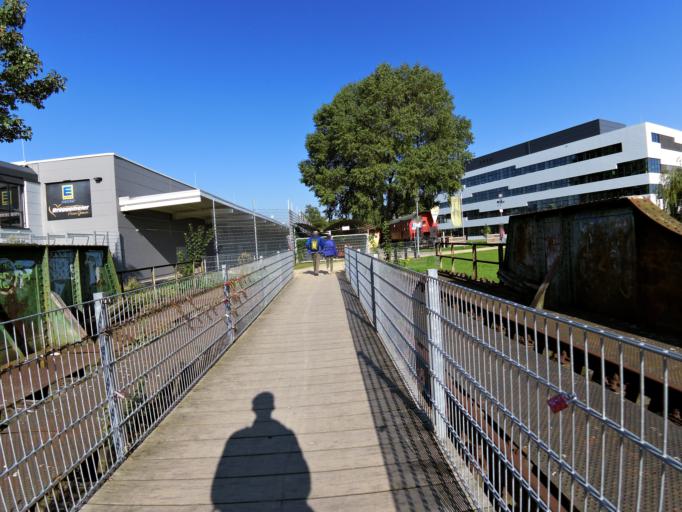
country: DE
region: North Rhine-Westphalia
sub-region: Regierungsbezirk Dusseldorf
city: Kleve
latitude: 51.7921
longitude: 6.1421
